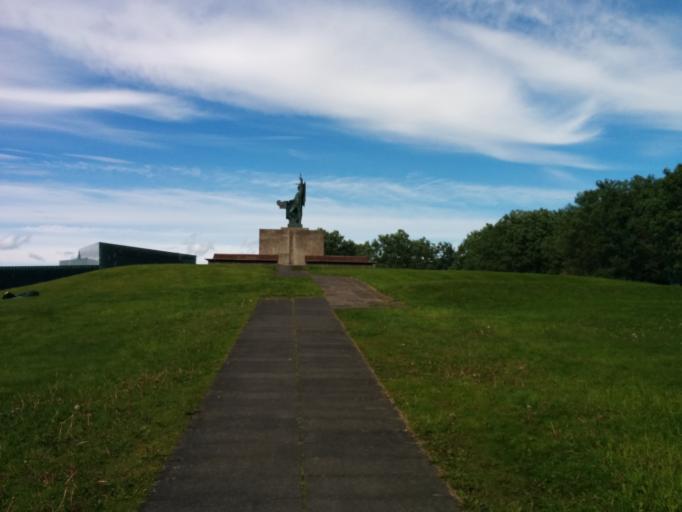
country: IS
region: Capital Region
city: Reykjavik
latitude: 64.1474
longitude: -21.9333
